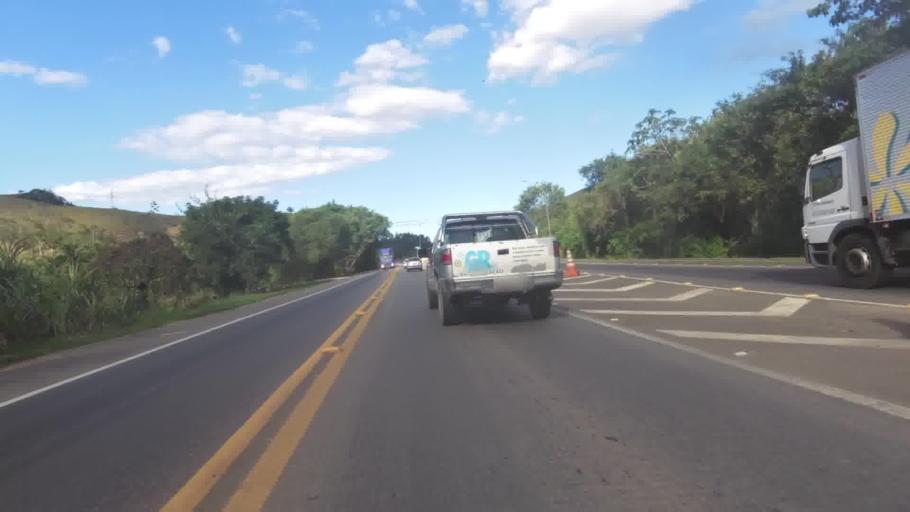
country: BR
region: Espirito Santo
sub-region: Rio Novo Do Sul
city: Rio Novo do Sul
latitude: -20.8655
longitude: -40.9161
